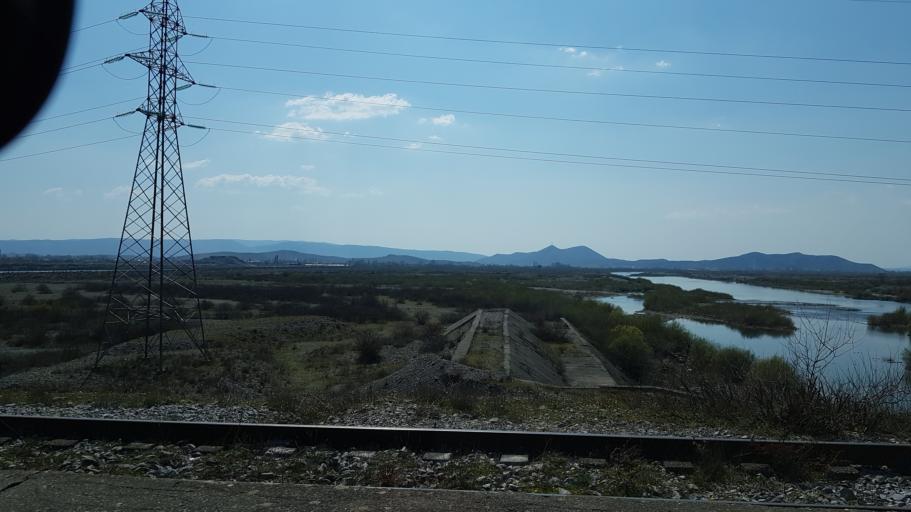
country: AL
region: Shkoder
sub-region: Rrethi i Shkodres
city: Vau i Dejes
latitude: 42.0060
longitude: 19.6001
